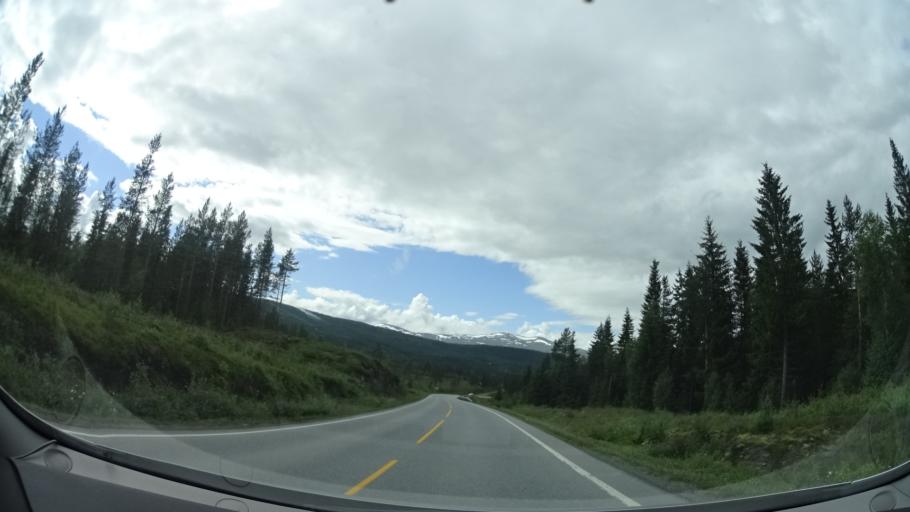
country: NO
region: Nord-Trondelag
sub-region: Meraker
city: Meraker
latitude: 63.3955
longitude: 11.8145
